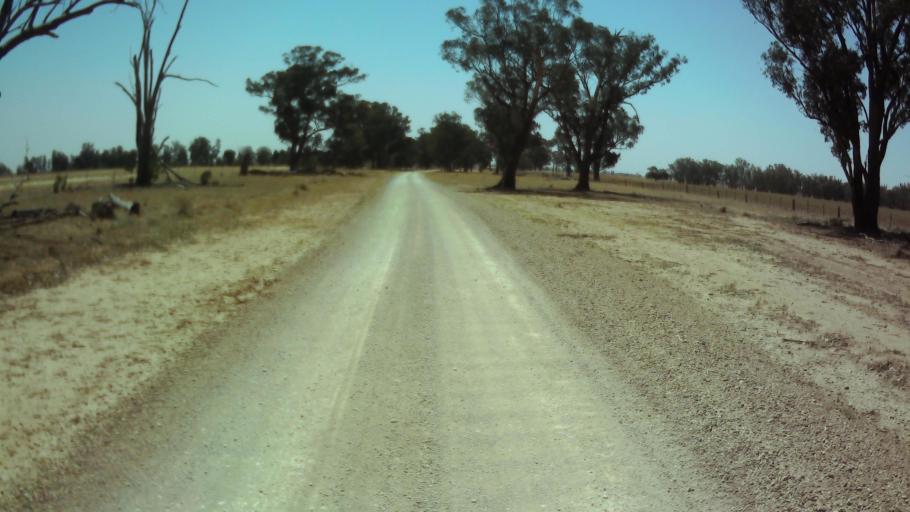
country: AU
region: New South Wales
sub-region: Weddin
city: Grenfell
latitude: -34.0185
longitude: 147.8994
